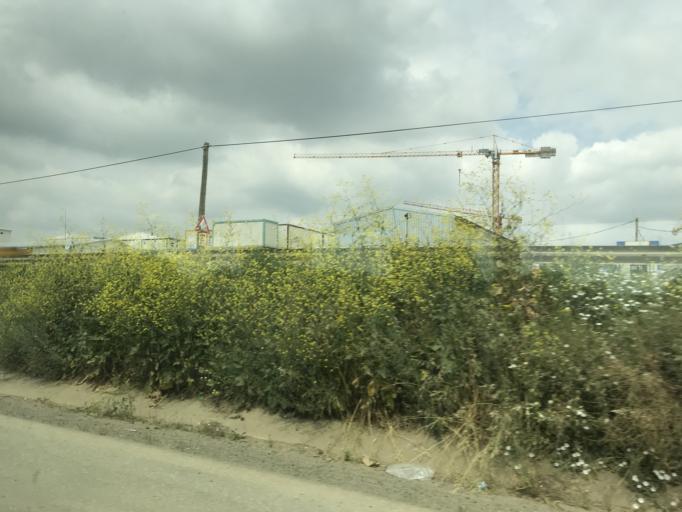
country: TR
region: Tekirdag
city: Tekirdag
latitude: 41.0059
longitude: 27.5262
